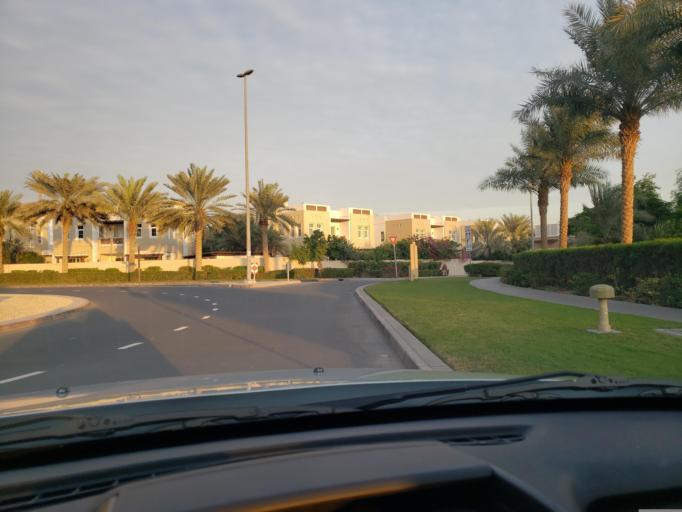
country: AE
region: Dubai
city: Dubai
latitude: 25.0201
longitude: 55.2737
